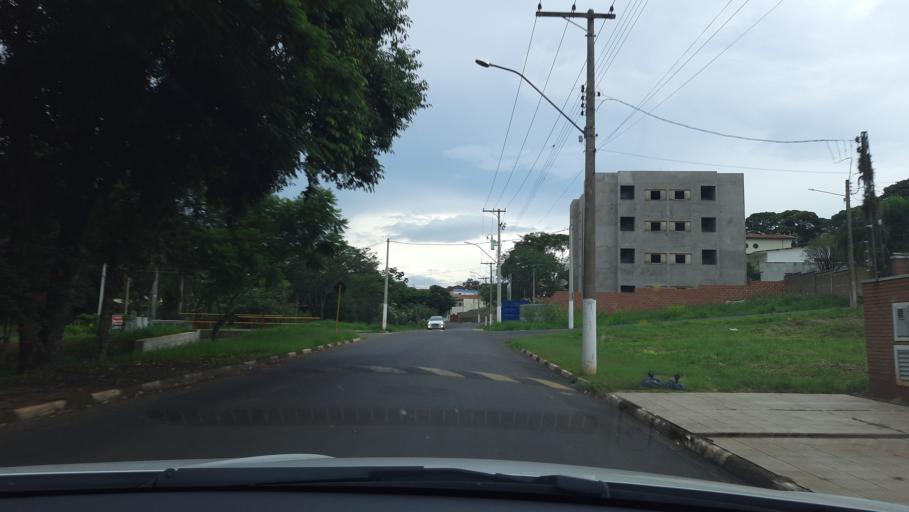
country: BR
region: Sao Paulo
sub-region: Casa Branca
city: Casa Branca
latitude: -21.7730
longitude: -47.0802
